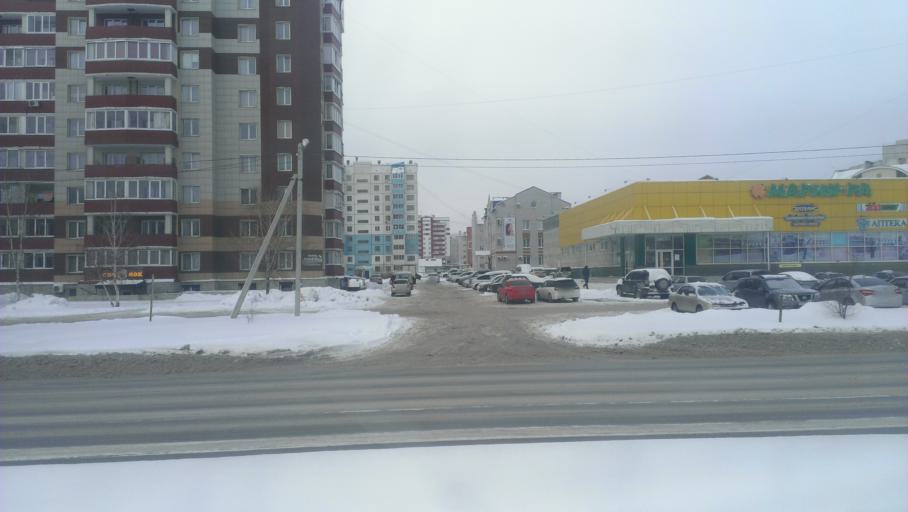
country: RU
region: Altai Krai
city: Novosilikatnyy
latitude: 53.3312
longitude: 83.6929
